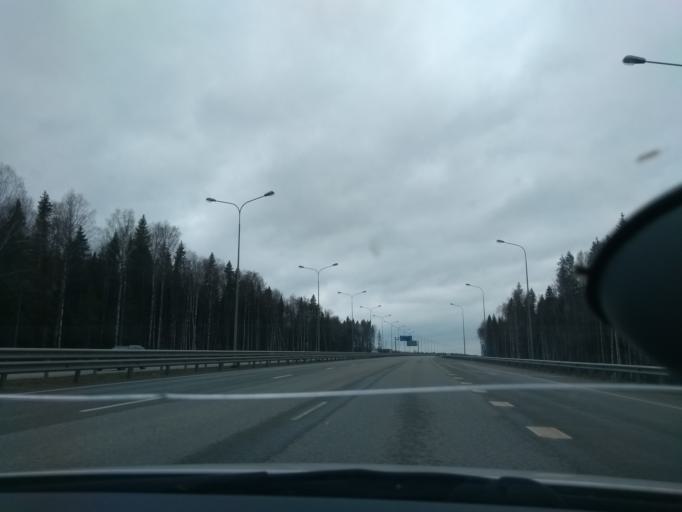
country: RU
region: Perm
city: Bershet'
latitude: 57.7008
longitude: 56.3773
